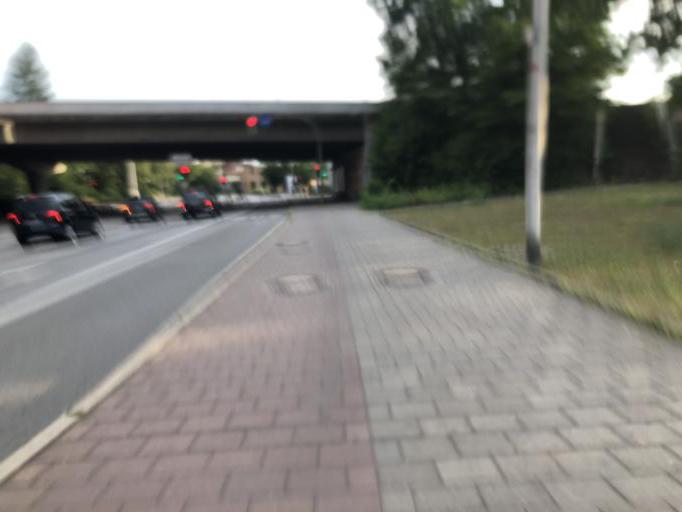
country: DE
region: Bavaria
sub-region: Regierungsbezirk Mittelfranken
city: Erlangen
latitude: 49.5910
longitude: 10.9978
